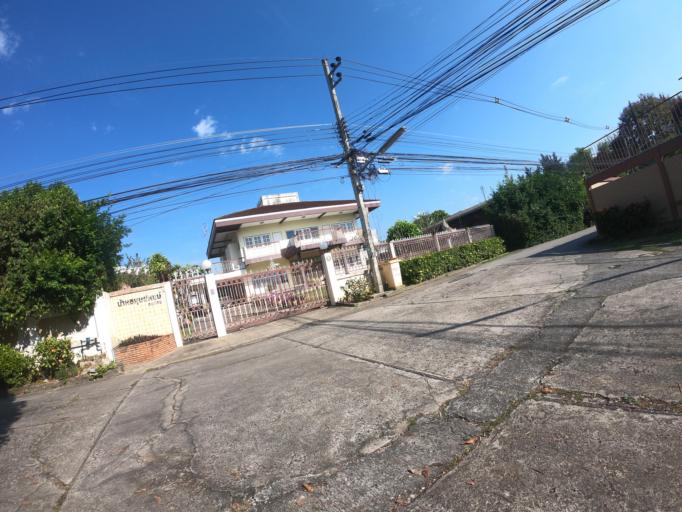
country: TH
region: Chiang Mai
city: Chiang Mai
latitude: 18.7927
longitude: 99.0158
